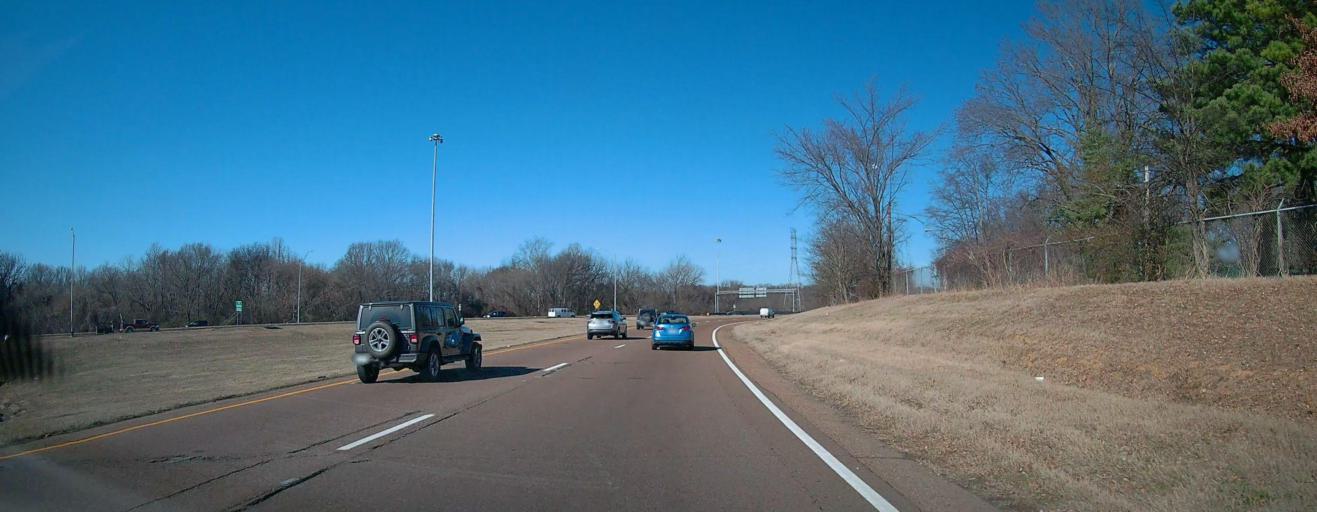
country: US
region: Tennessee
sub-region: Shelby County
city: Bartlett
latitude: 35.1938
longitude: -89.9245
